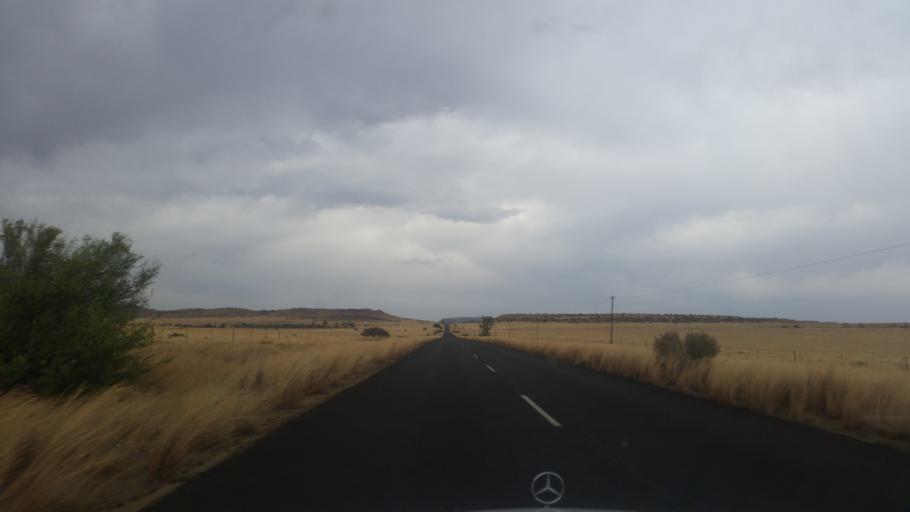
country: ZA
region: Orange Free State
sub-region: Xhariep District Municipality
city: Trompsburg
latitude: -30.4240
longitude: 26.1394
